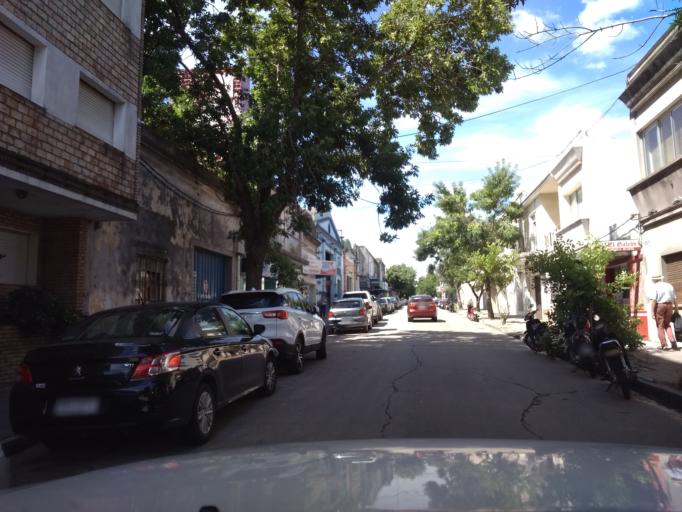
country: UY
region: Florida
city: Florida
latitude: -34.0990
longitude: -56.2163
